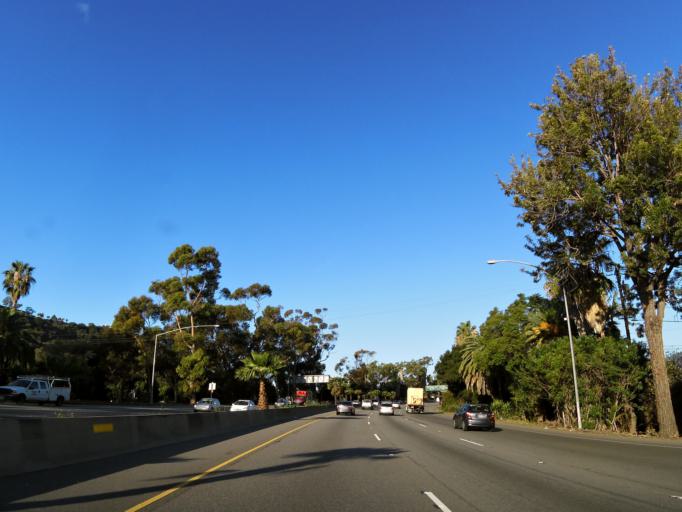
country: US
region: California
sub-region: Santa Barbara County
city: Santa Barbara
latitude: 34.4124
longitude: -119.7014
